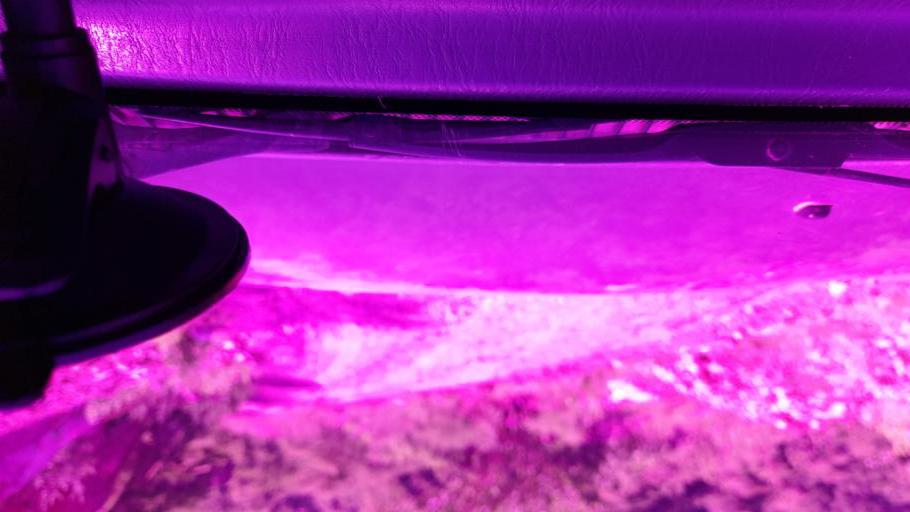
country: ET
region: Oromiya
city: Jima
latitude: 7.8024
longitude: 37.5258
